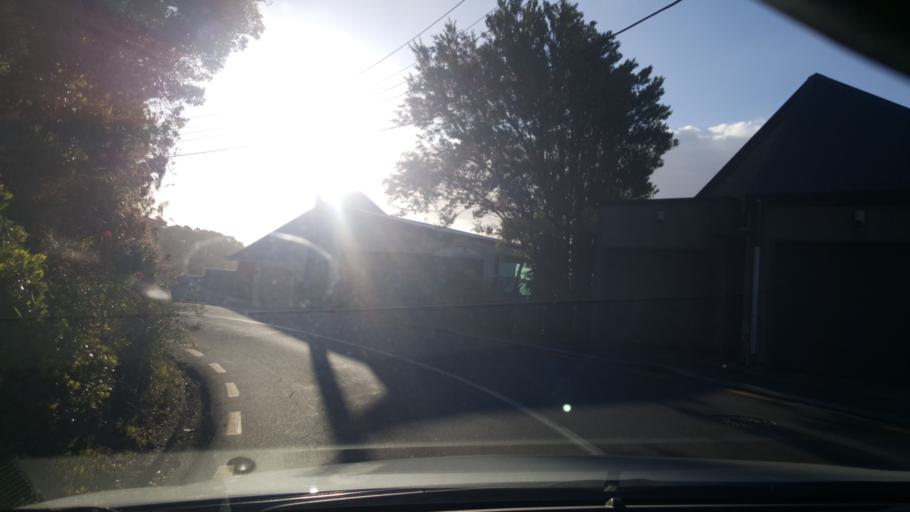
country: NZ
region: Wellington
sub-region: Wellington City
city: Wellington
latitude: -41.2933
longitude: 174.7980
